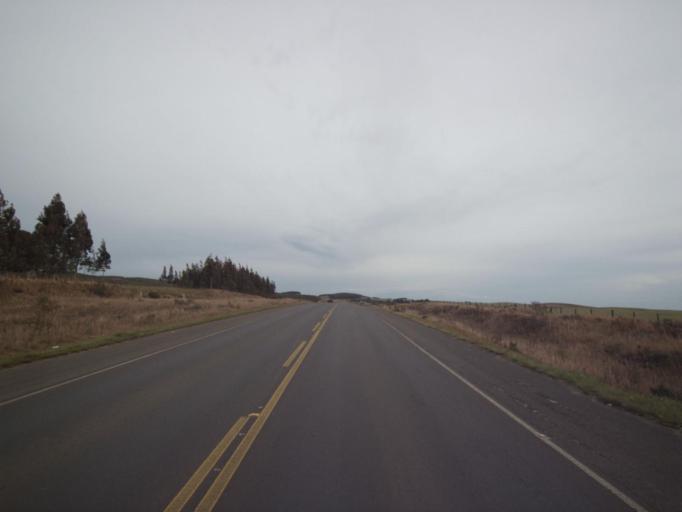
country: BR
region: Parana
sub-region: Palmas
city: Palmas
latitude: -26.7362
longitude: -51.6488
